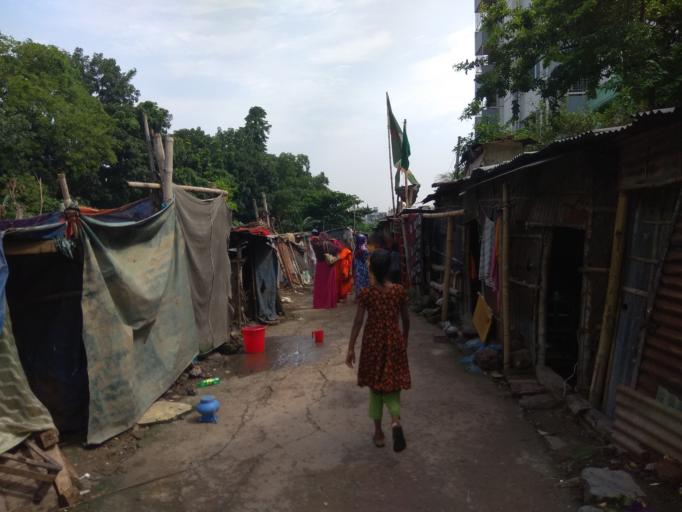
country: BD
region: Dhaka
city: Azimpur
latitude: 23.8103
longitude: 90.3546
